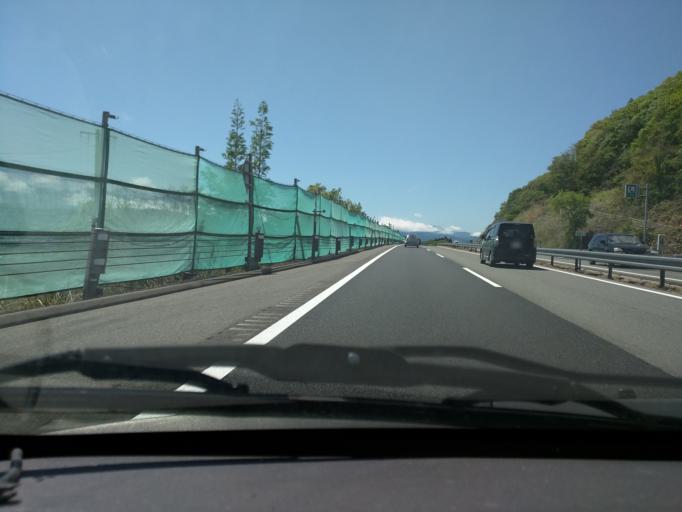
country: JP
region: Nagano
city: Nakano
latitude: 36.7641
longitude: 138.3160
